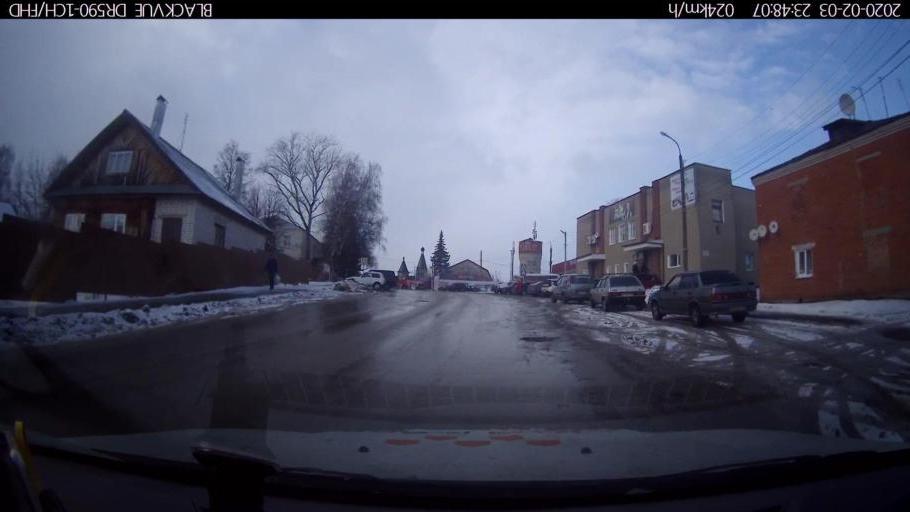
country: RU
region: Nizjnij Novgorod
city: Dal'neye Konstantinovo
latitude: 55.8112
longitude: 44.0957
